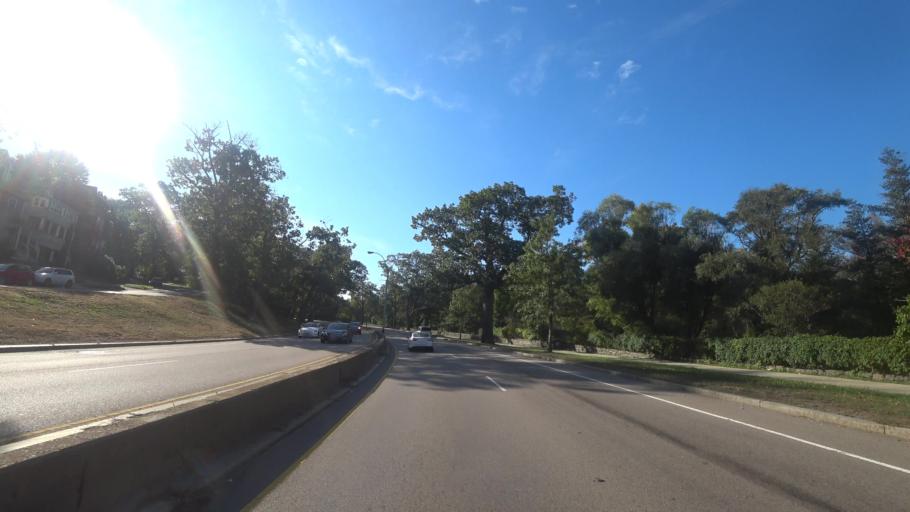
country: US
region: Massachusetts
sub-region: Suffolk County
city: Jamaica Plain
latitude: 42.3053
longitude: -71.1200
